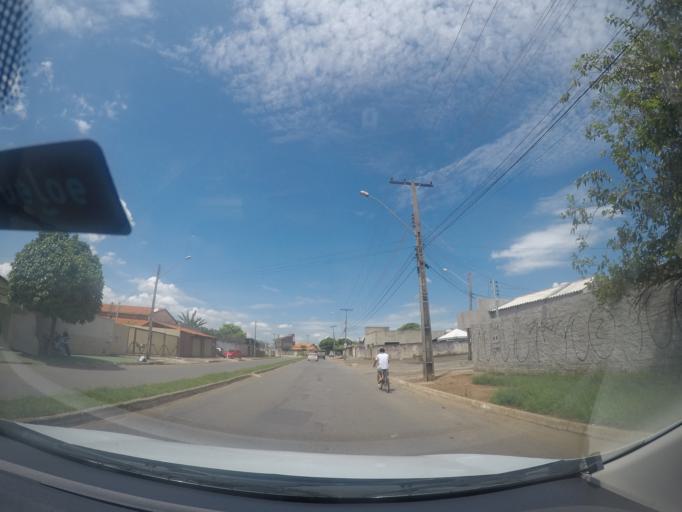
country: BR
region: Goias
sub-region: Goiania
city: Goiania
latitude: -16.6870
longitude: -49.3484
